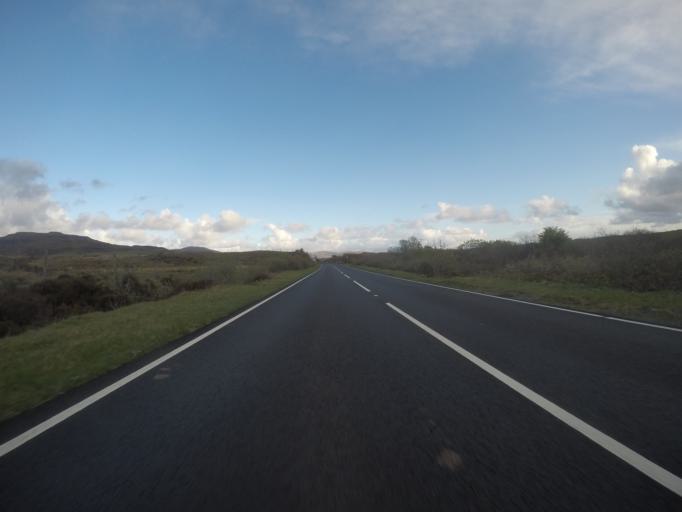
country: GB
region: Scotland
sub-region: Highland
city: Portree
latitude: 57.5022
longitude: -6.3297
